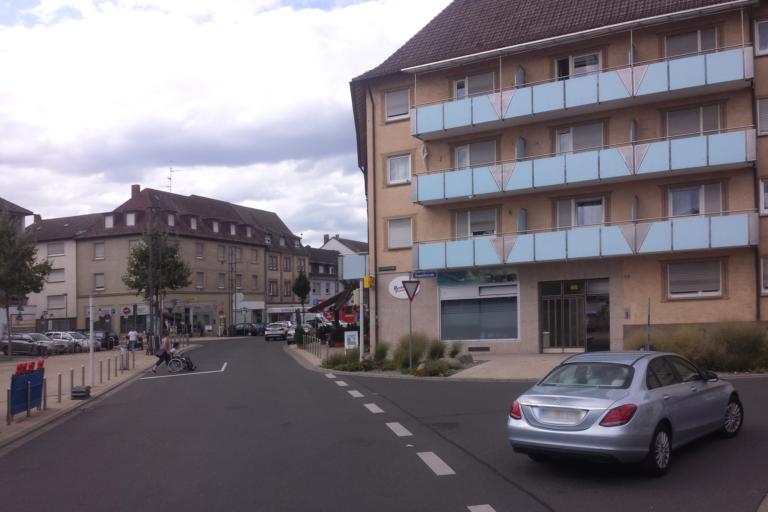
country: DE
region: Baden-Wuerttemberg
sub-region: Karlsruhe Region
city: Mannheim
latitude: 49.5425
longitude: 8.4489
